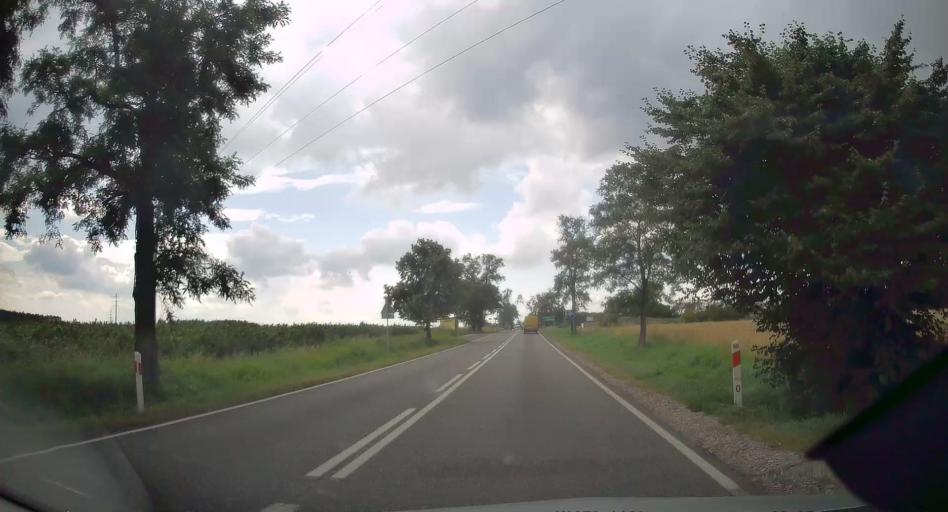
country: PL
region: Lodz Voivodeship
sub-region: Powiat skierniewicki
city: Gluchow
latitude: 51.7758
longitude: 20.1215
